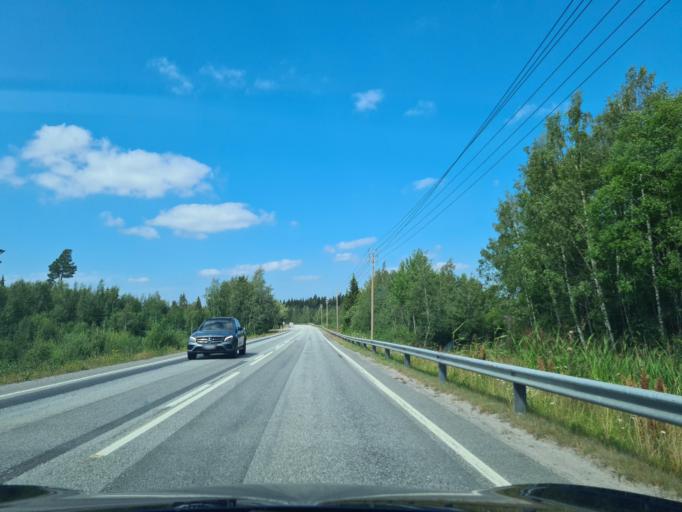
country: FI
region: Ostrobothnia
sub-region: Vaasa
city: Vaasa
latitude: 63.1869
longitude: 21.5661
